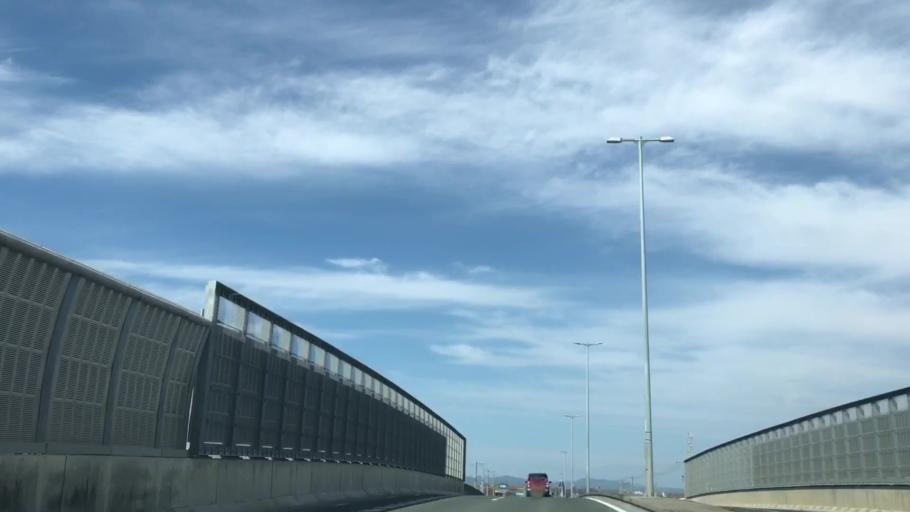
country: JP
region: Shizuoka
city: Hamamatsu
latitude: 34.6850
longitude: 137.6477
